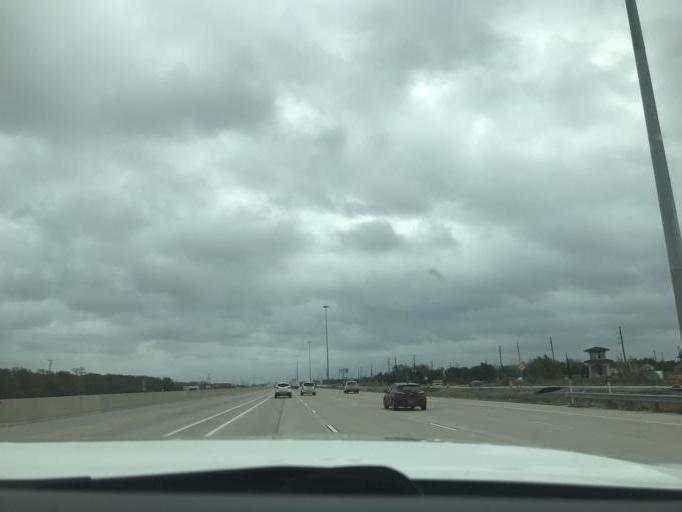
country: US
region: Texas
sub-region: Fort Bend County
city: Greatwood
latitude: 29.5580
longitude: -95.7061
